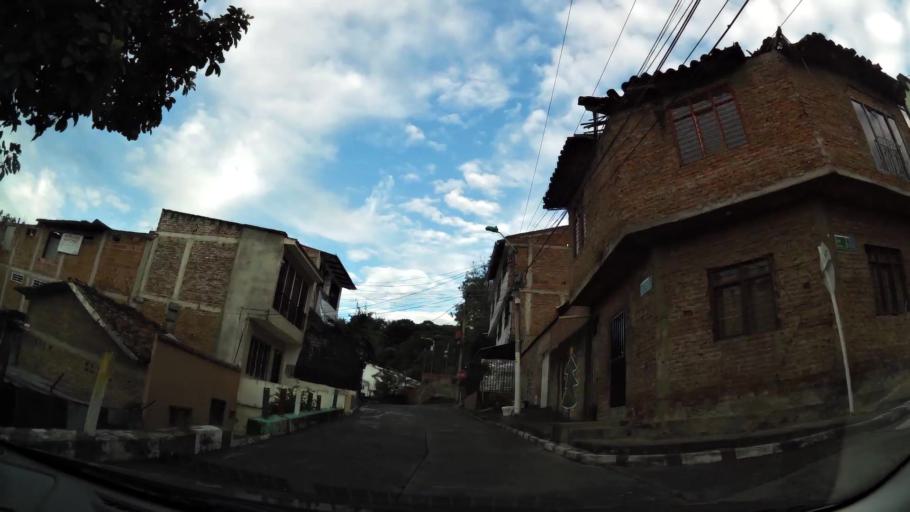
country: CO
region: Valle del Cauca
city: Cali
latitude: 3.4452
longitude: -76.5427
